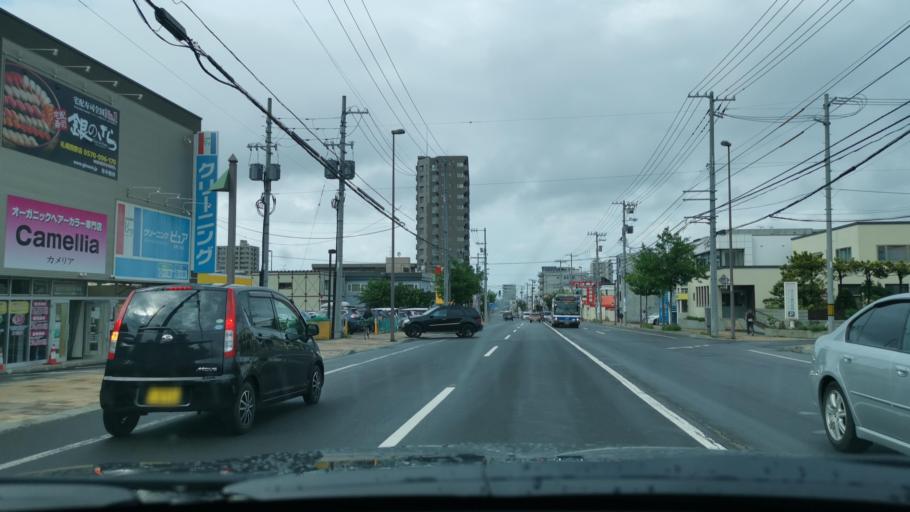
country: JP
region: Hokkaido
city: Sapporo
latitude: 43.0765
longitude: 141.2847
